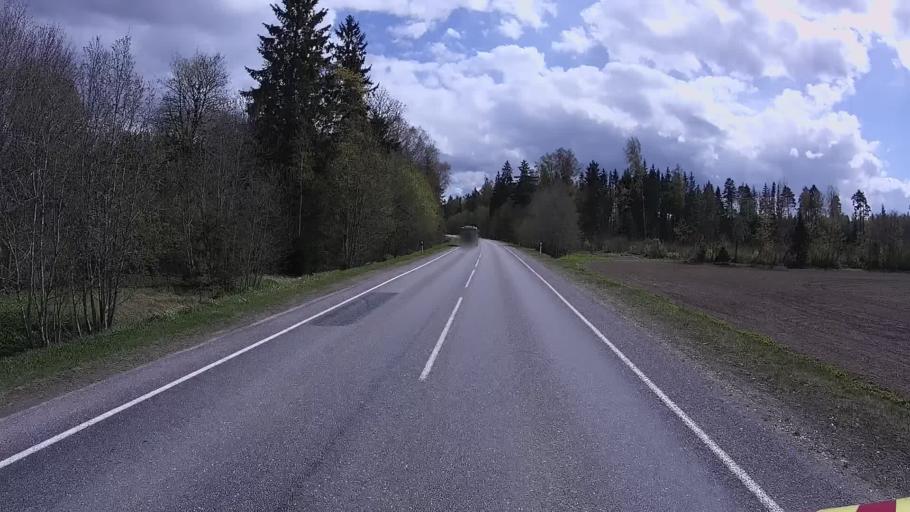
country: EE
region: Jaervamaa
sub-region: Jaerva-Jaani vald
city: Jarva-Jaani
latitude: 59.0987
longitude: 25.8182
